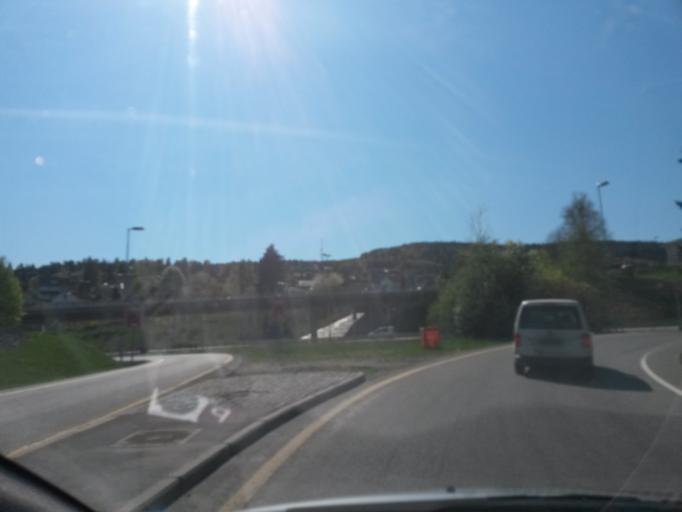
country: NO
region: Buskerud
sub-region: Drammen
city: Drammen
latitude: 59.7292
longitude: 10.2172
